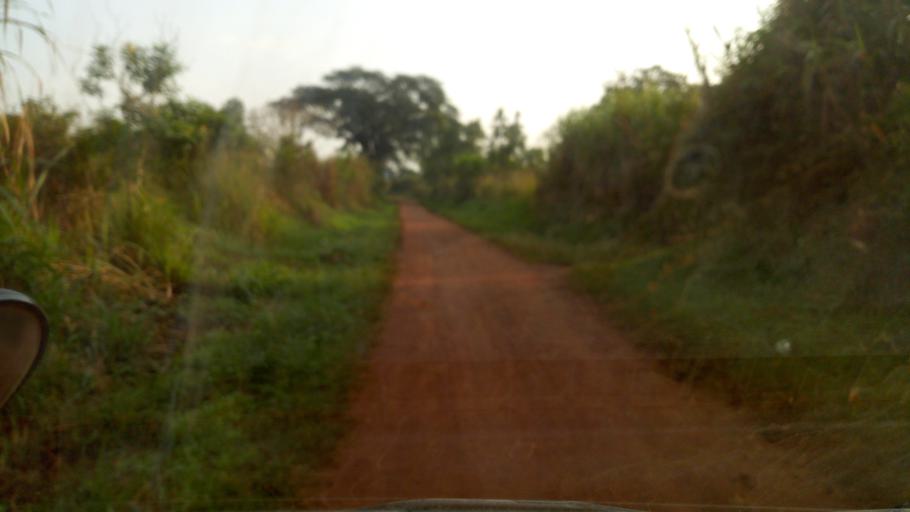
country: UG
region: Western Region
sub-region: Masindi District
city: Masindi
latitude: 1.7672
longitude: 31.8395
